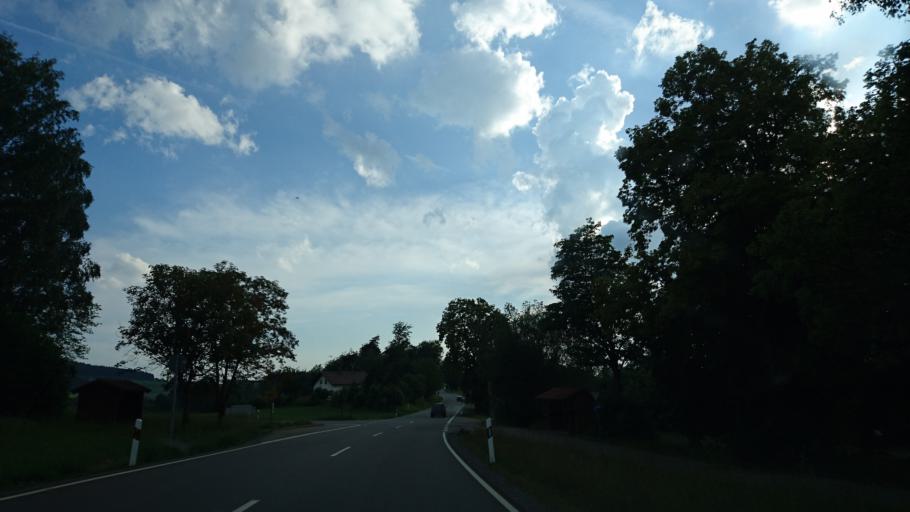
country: DE
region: Bavaria
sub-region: Lower Bavaria
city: Neuschonau
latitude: 48.8721
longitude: 13.4718
